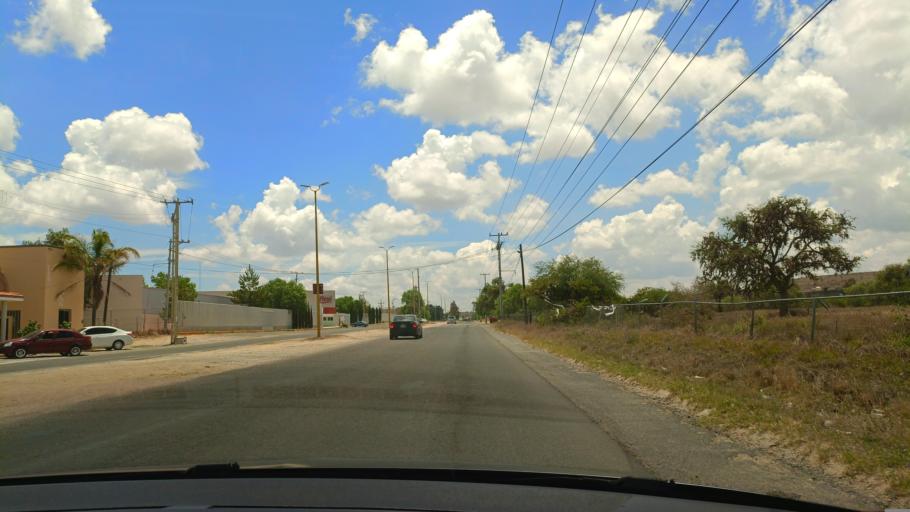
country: MX
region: Guanajuato
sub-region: San Luis de la Paz
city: San Ignacio
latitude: 21.2875
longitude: -100.5424
